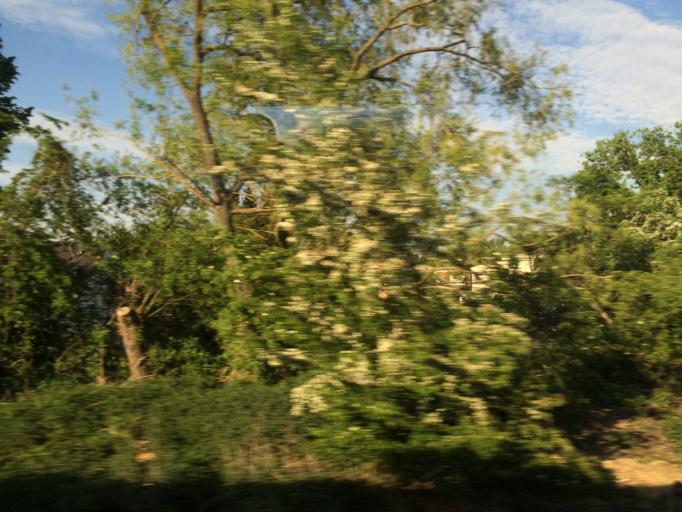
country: DE
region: North Rhine-Westphalia
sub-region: Regierungsbezirk Dusseldorf
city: Erkrath
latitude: 51.1853
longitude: 6.8570
